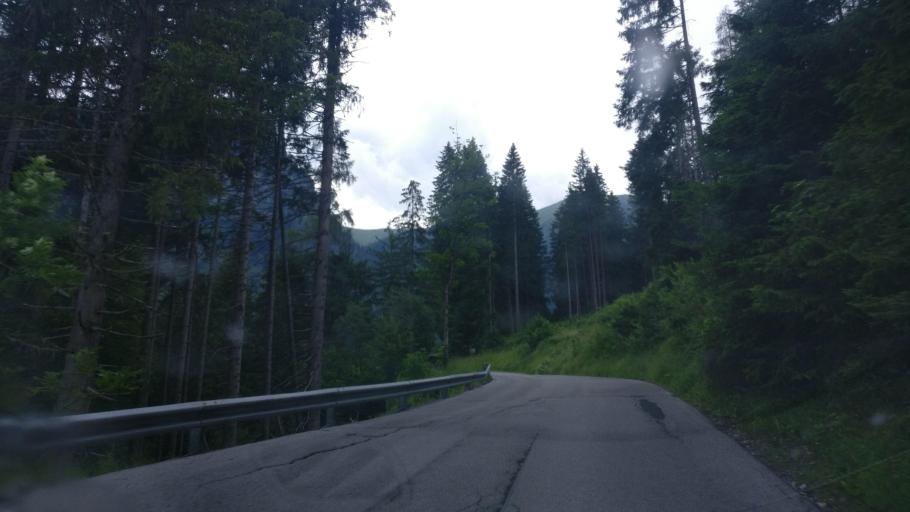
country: AT
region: Salzburg
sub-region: Politischer Bezirk Sankt Johann im Pongau
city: Bad Gastein
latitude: 47.1249
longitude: 13.1487
